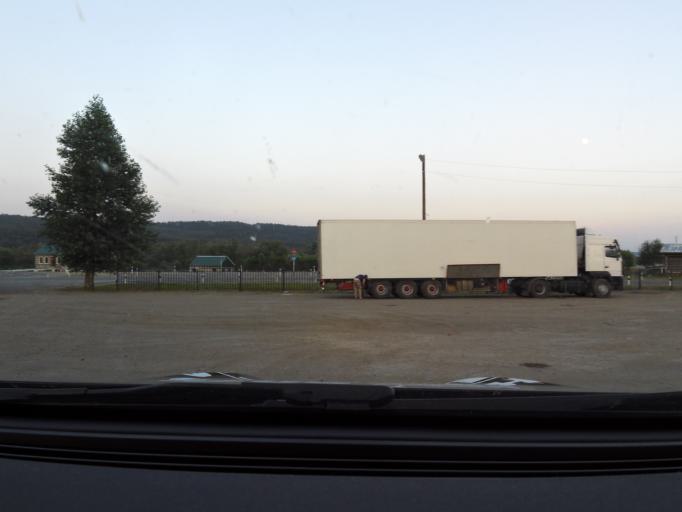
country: RU
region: Sverdlovsk
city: Arti
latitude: 56.3703
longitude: 58.5657
